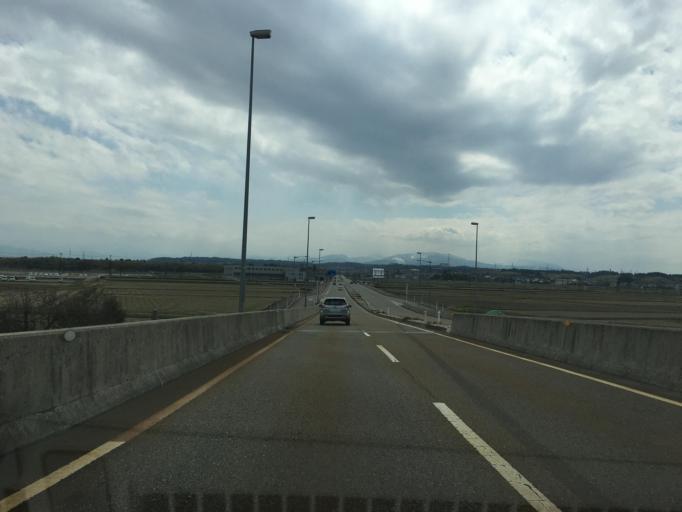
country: JP
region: Toyama
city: Kuragaki-kosugi
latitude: 36.7149
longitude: 137.1180
